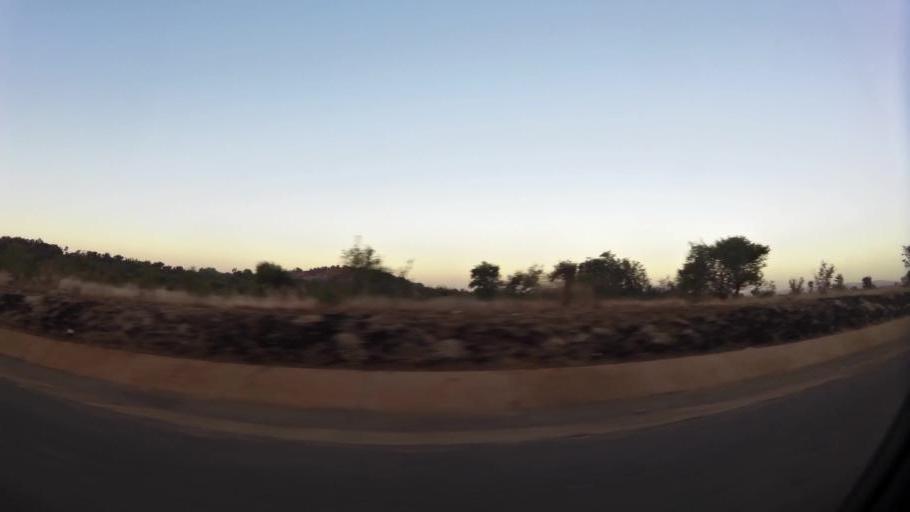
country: ZA
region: North-West
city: Ga-Rankuwa
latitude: -25.6076
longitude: 28.0390
